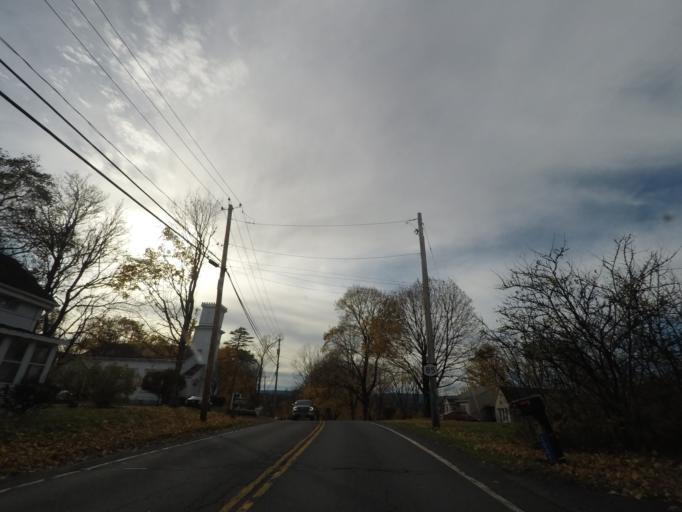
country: US
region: New York
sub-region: Albany County
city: Voorheesville
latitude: 42.6320
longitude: -73.9057
